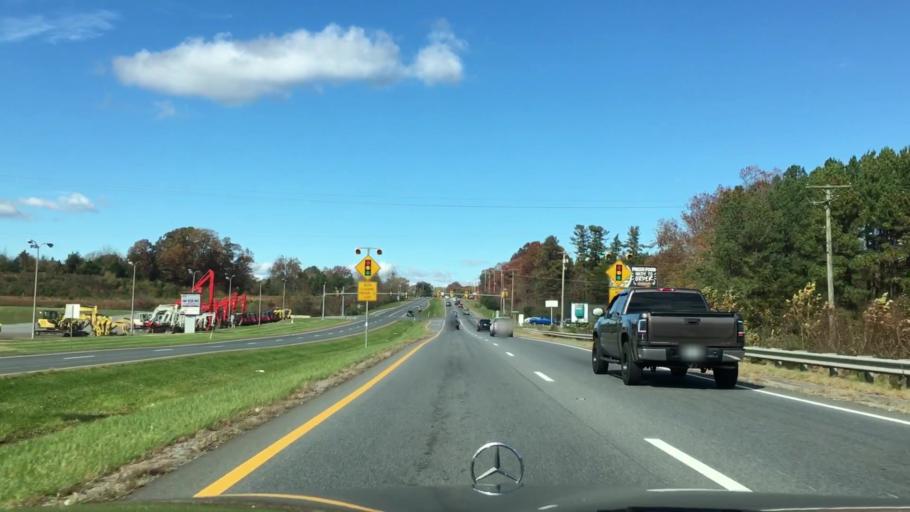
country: US
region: Virginia
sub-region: Campbell County
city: Timberlake
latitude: 37.3107
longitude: -79.1829
